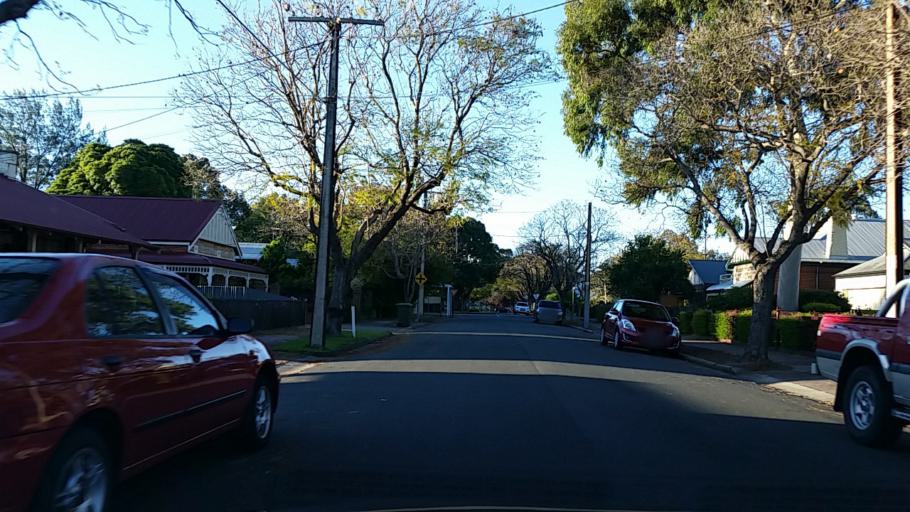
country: AU
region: South Australia
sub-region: Mitcham
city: Clarence Gardens
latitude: -34.9634
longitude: 138.5759
